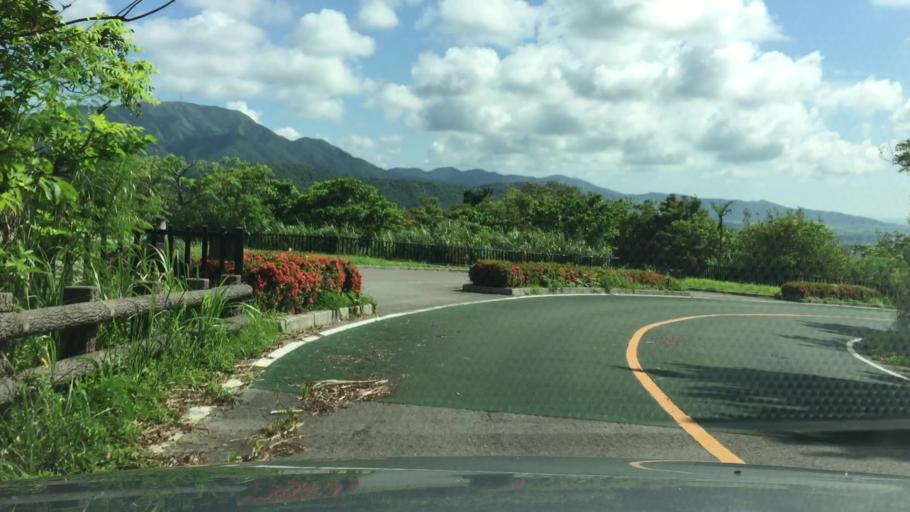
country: JP
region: Okinawa
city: Ishigaki
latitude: 24.3843
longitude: 124.1691
